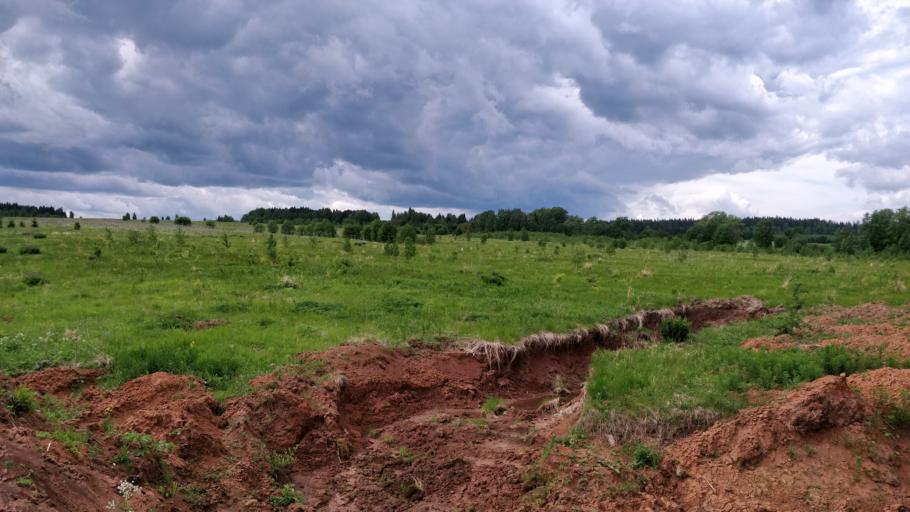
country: RU
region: Perm
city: Ust'-Kachka
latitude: 57.9382
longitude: 55.6843
